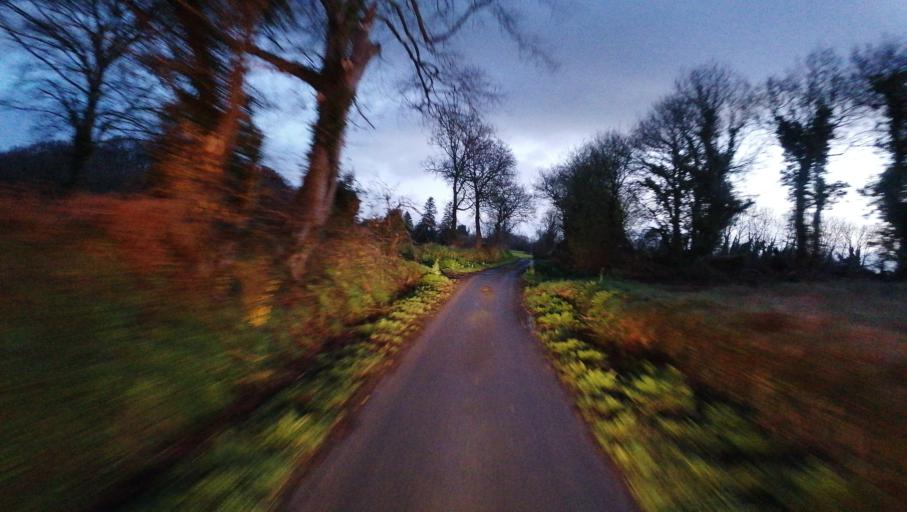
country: FR
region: Brittany
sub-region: Departement des Cotes-d'Armor
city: Lanvollon
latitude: 48.6641
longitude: -2.9668
